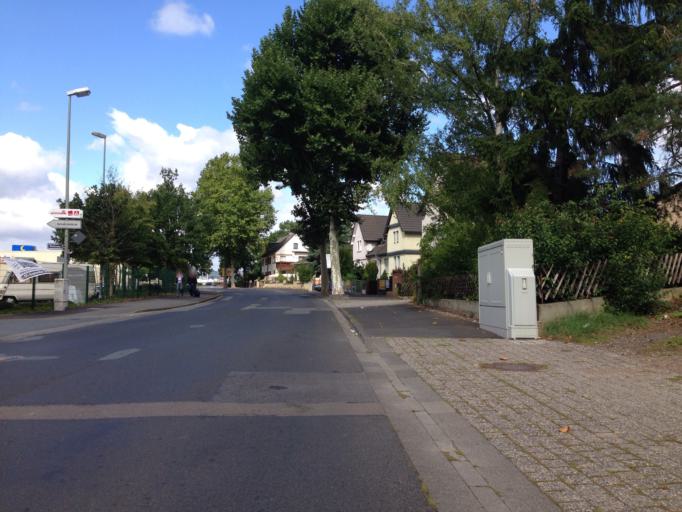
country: DE
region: Hesse
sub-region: Regierungsbezirk Giessen
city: Limburg an der Lahn
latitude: 50.3968
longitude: 8.0590
